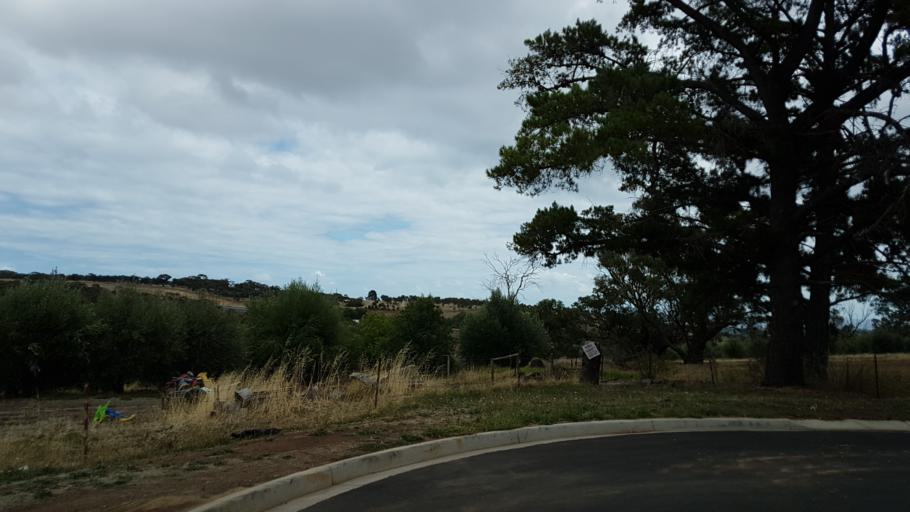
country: AU
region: South Australia
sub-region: Onkaparinga
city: Bedford Park
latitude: -35.0414
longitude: 138.5645
